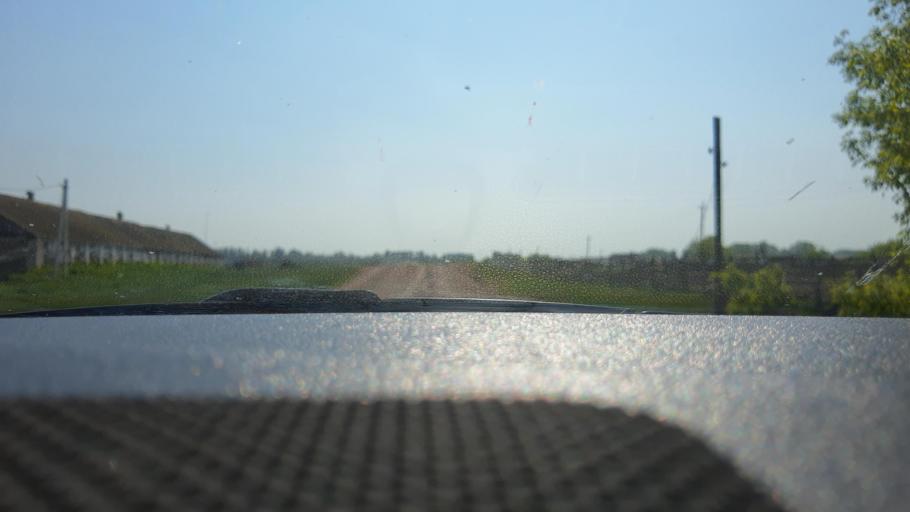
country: RU
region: Bashkortostan
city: Chishmy
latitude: 54.4451
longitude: 55.3164
